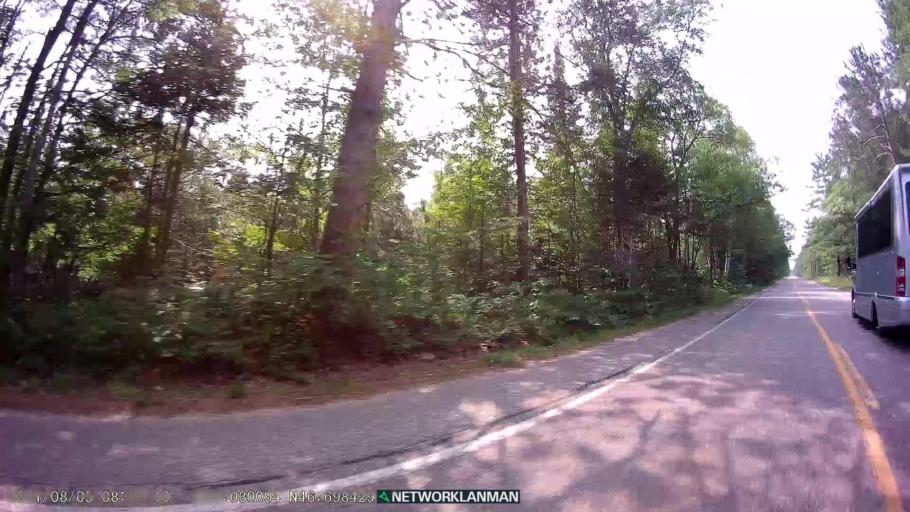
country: US
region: Michigan
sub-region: Luce County
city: Newberry
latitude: 46.6982
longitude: -85.0303
